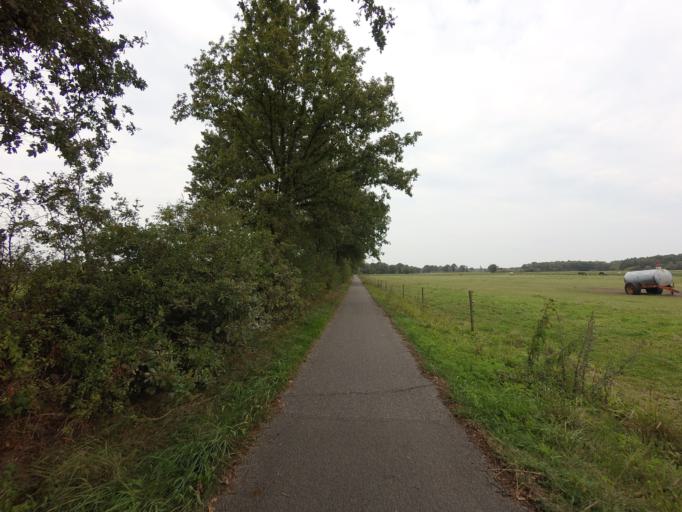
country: NL
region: Drenthe
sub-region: Gemeente Assen
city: Assen
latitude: 53.0030
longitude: 6.6342
